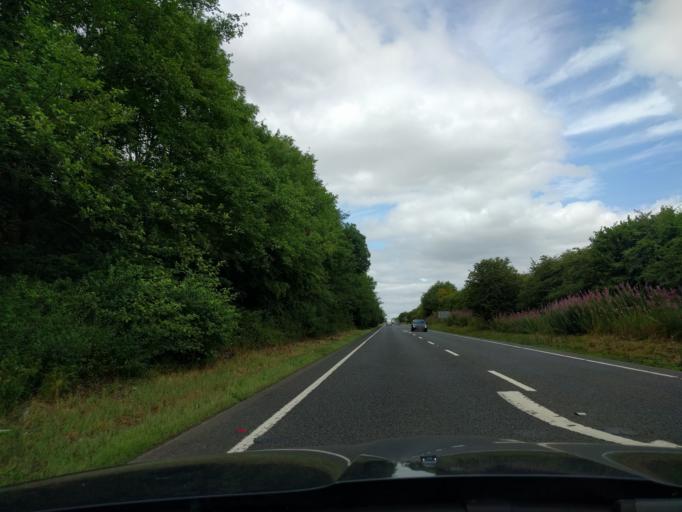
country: GB
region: England
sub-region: Northumberland
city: Alnwick
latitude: 55.4346
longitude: -1.6925
